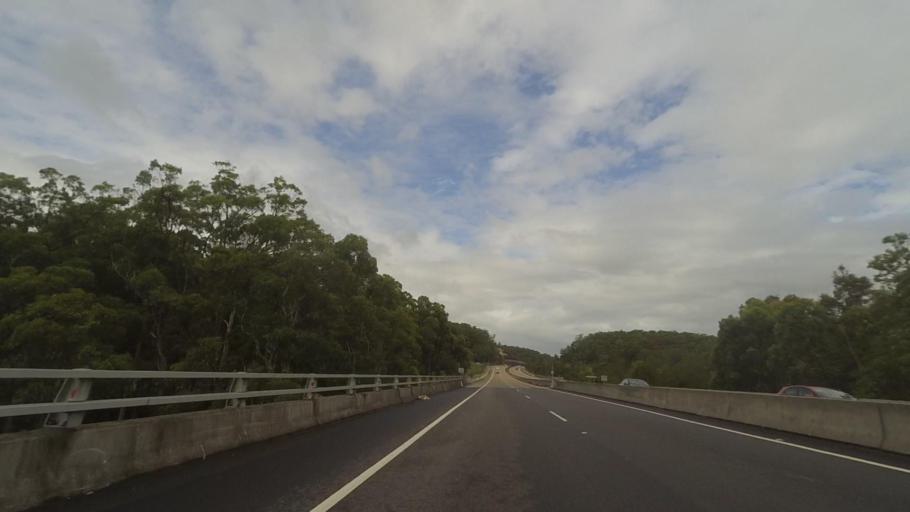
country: AU
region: New South Wales
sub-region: Port Stephens Shire
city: Port Stephens
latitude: -32.6212
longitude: 151.9622
